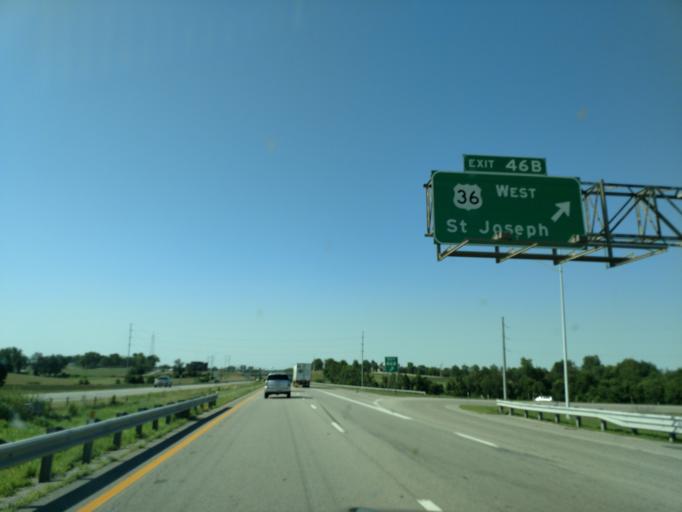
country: US
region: Missouri
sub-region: Buchanan County
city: Saint Joseph
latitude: 39.7496
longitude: -94.7895
